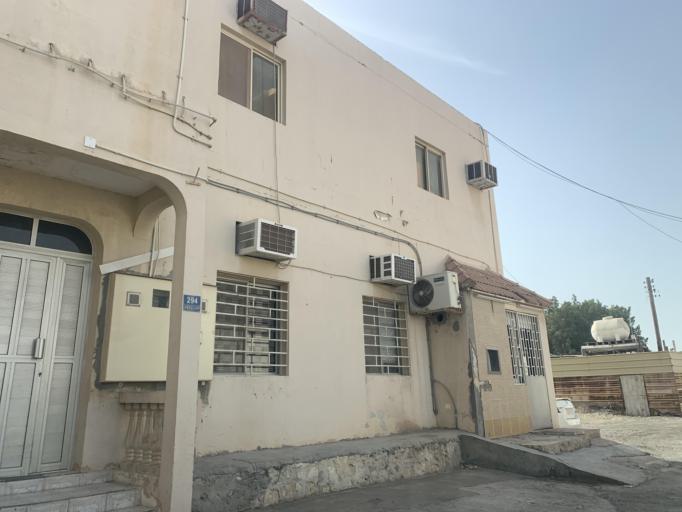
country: BH
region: Northern
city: Madinat `Isa
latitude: 26.1637
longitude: 50.5159
